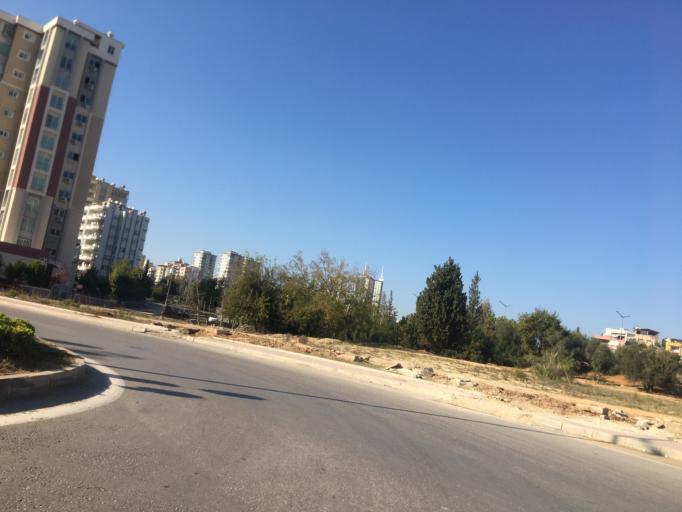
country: TR
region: Adana
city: Seyhan
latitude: 37.0289
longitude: 35.2706
